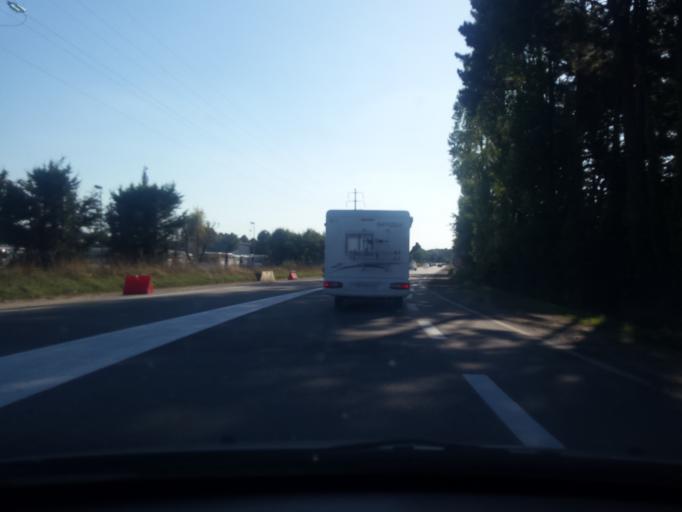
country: FR
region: Brittany
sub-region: Departement du Morbihan
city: Saint-Ave
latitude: 47.6824
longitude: -2.7678
